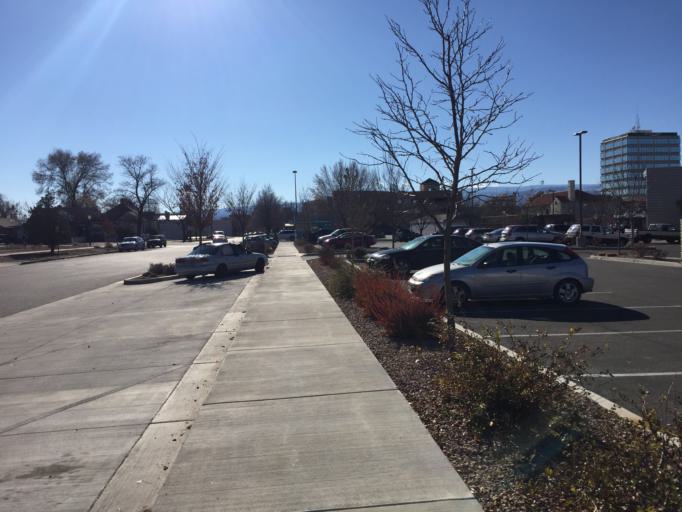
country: US
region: Colorado
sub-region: Mesa County
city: Grand Junction
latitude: 39.0712
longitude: -108.5629
